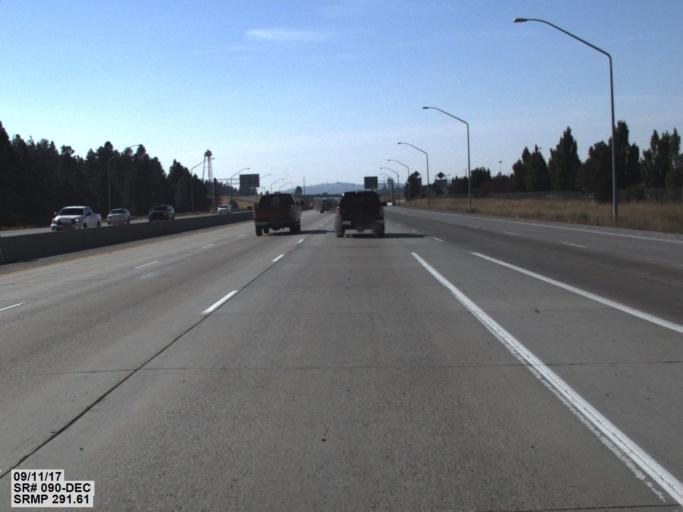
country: US
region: Washington
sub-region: Spokane County
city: Veradale
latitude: 47.6705
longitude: -117.2027
